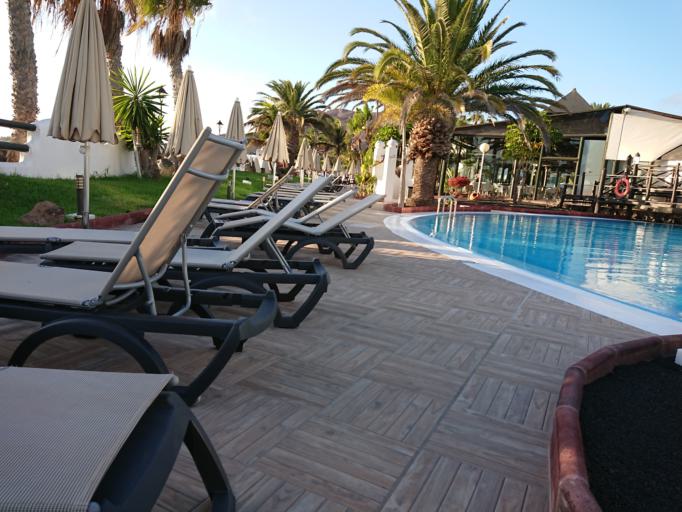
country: ES
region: Canary Islands
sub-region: Provincia de Las Palmas
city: Playa Blanca
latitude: 28.8596
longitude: -13.8450
